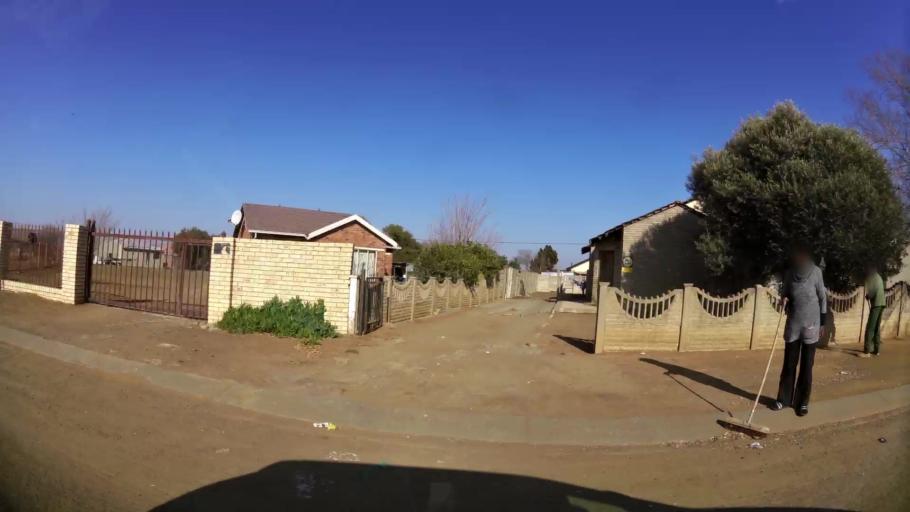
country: ZA
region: Orange Free State
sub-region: Mangaung Metropolitan Municipality
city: Bloemfontein
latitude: -29.1806
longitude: 26.1798
